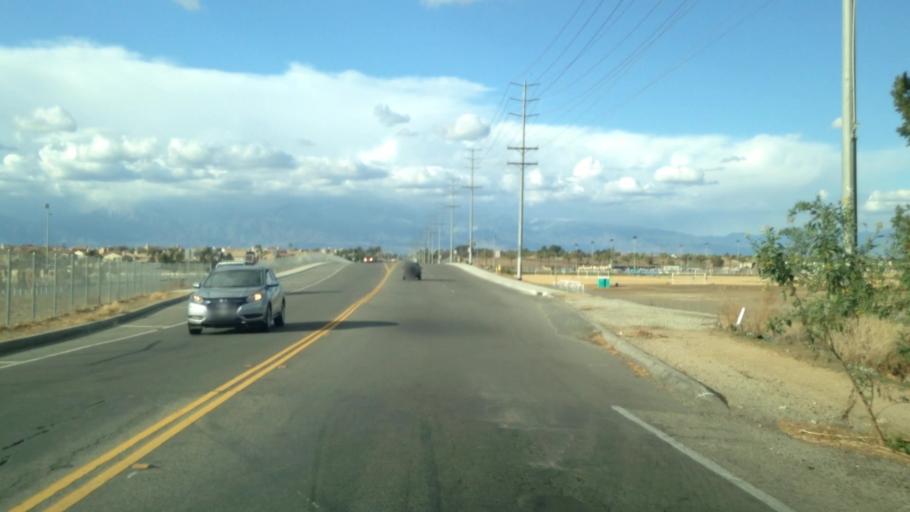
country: US
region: California
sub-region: Riverside County
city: Norco
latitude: 33.9475
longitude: -117.5583
